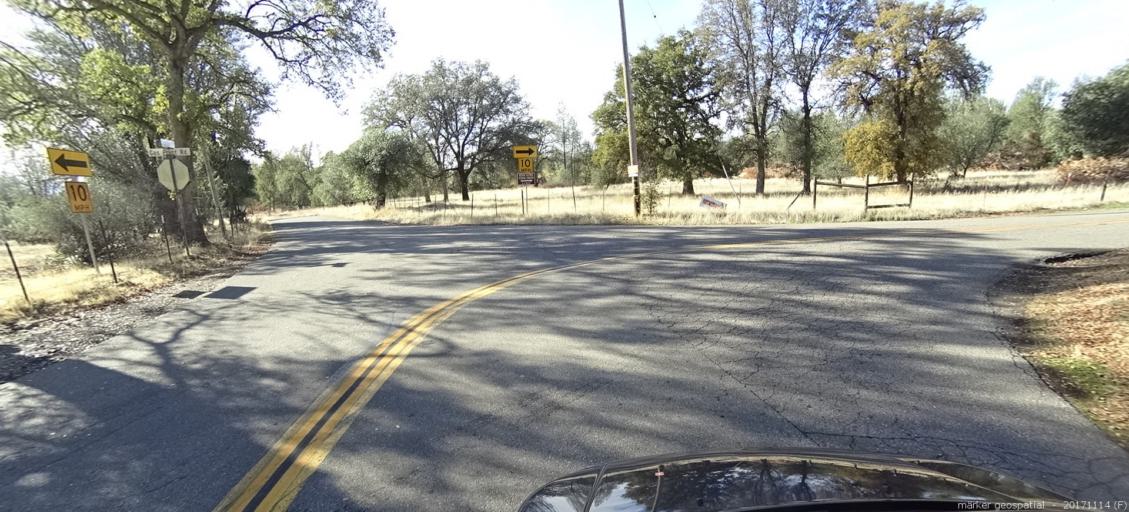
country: US
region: California
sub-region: Shasta County
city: Shasta
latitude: 40.3988
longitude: -122.5203
